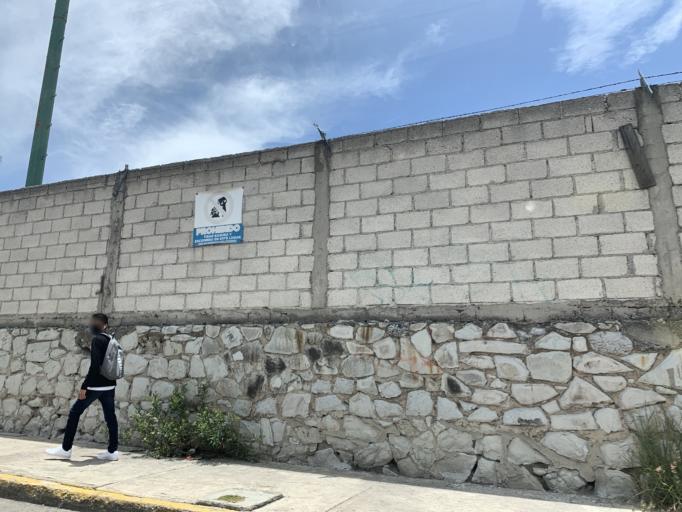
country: MX
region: Puebla
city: Puebla
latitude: 19.0773
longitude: -98.2084
